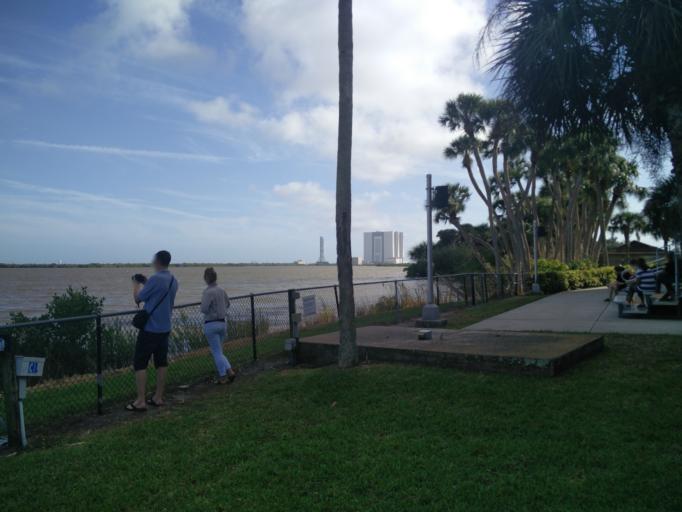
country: US
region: Florida
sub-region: Brevard County
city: Merritt Island
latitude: 28.6054
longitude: -80.6690
